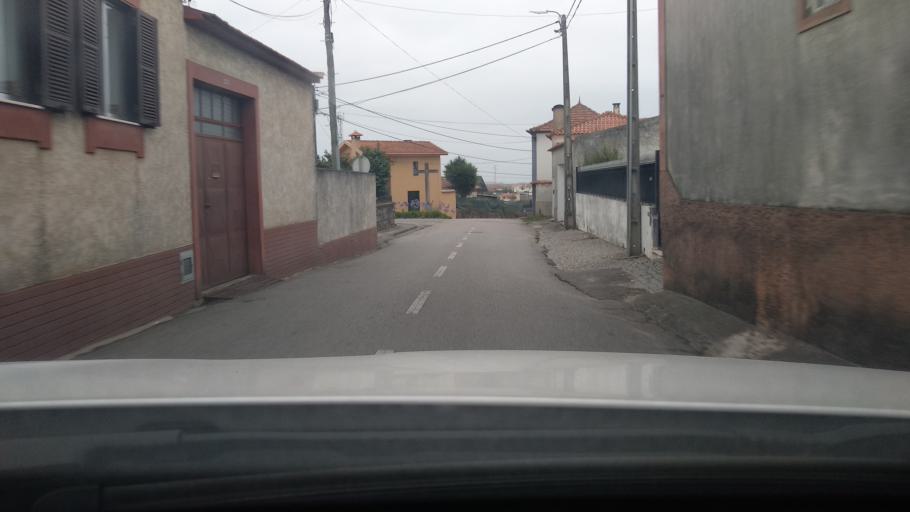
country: PT
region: Aveiro
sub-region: Espinho
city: Souto
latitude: 40.9784
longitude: -8.6294
